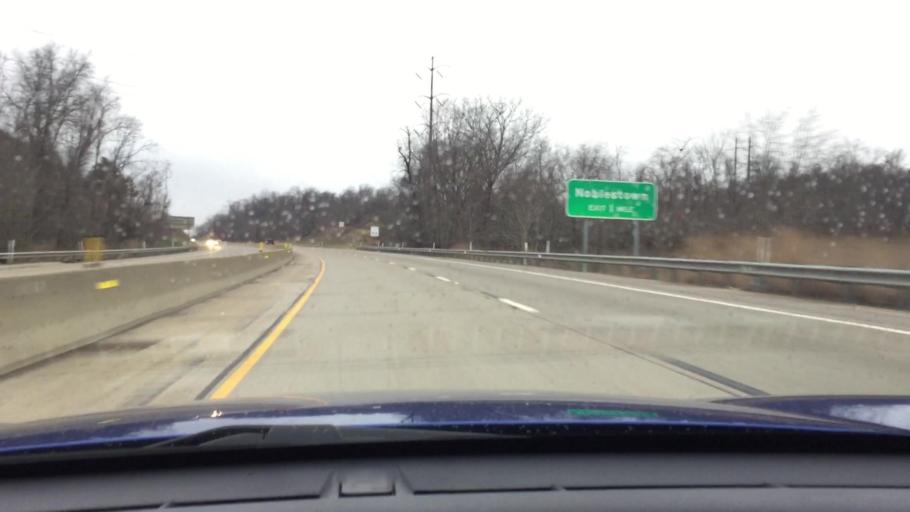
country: US
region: Pennsylvania
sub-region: Allegheny County
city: Imperial
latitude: 40.4386
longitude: -80.2445
